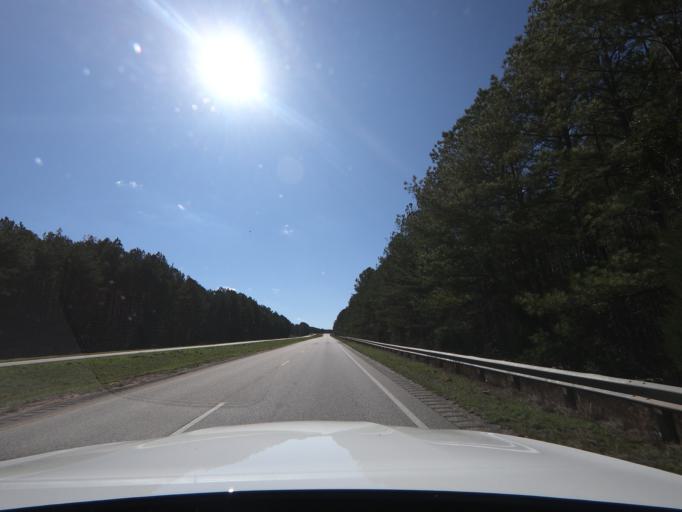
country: US
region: Alabama
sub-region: Henry County
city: Abbeville
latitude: 31.7352
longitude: -85.2528
